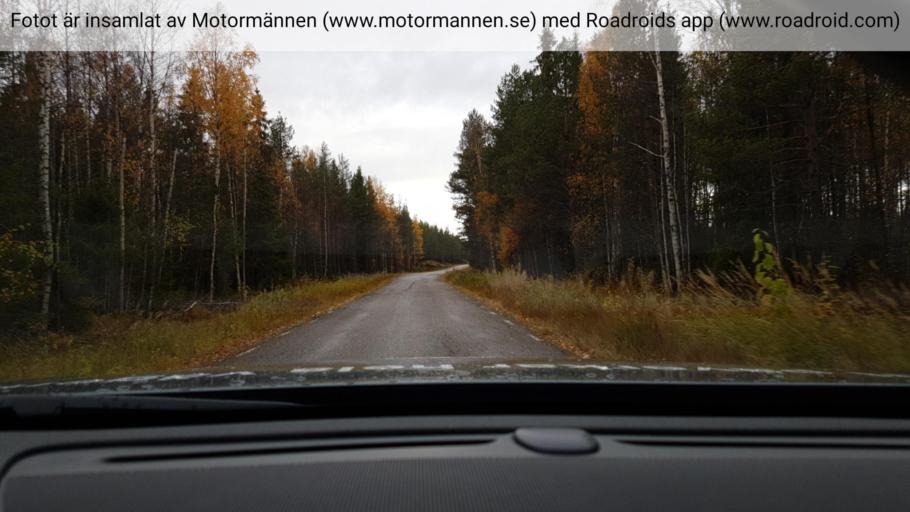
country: SE
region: Norrbotten
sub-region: Pajala Kommun
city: Pajala
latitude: 67.1776
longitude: 22.6953
